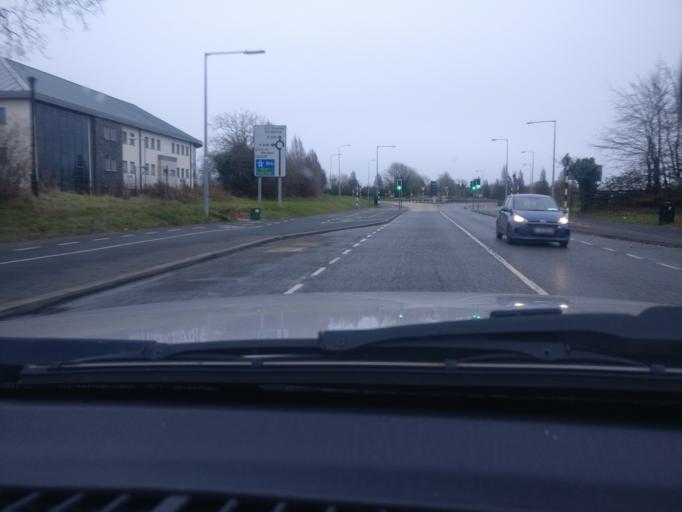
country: IE
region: Leinster
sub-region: Kildare
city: Celbridge
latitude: 53.3584
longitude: -6.5502
